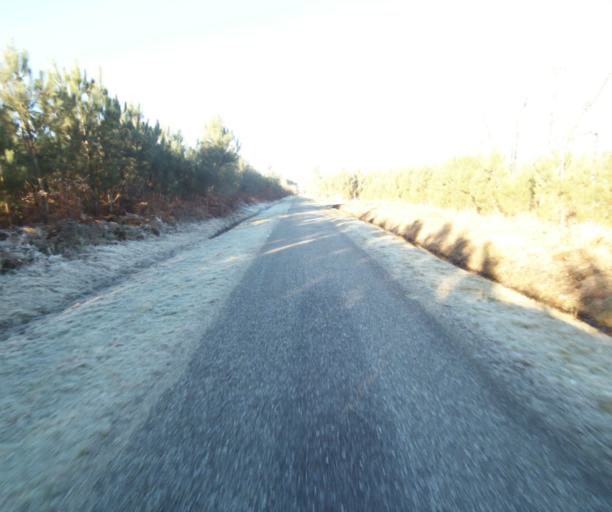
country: FR
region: Aquitaine
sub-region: Departement des Landes
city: Gabarret
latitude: 44.1099
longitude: 0.0548
